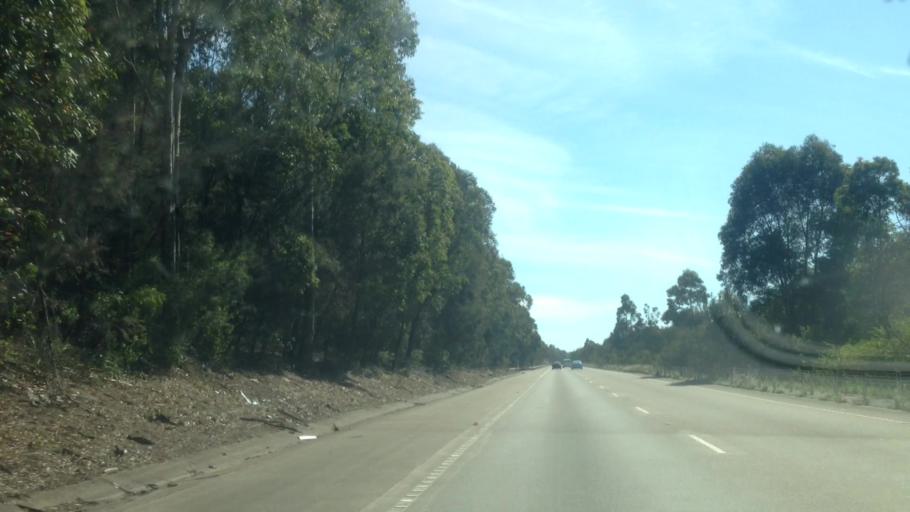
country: AU
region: New South Wales
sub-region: Lake Macquarie Shire
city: Fennell Bay
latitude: -32.9676
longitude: 151.5357
